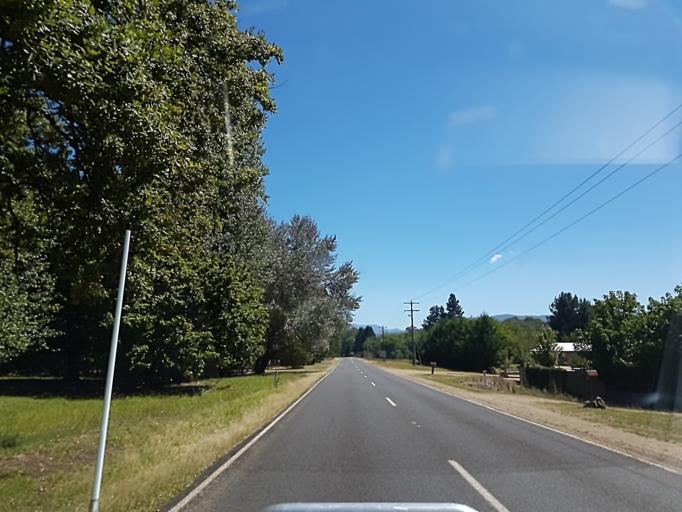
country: AU
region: Victoria
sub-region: Alpine
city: Mount Beauty
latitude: -36.7738
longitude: 147.0304
